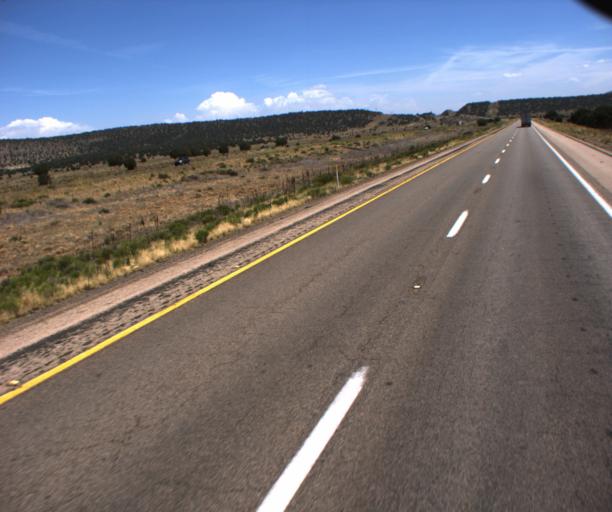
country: US
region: Arizona
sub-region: Mohave County
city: Peach Springs
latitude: 35.2304
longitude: -113.2222
